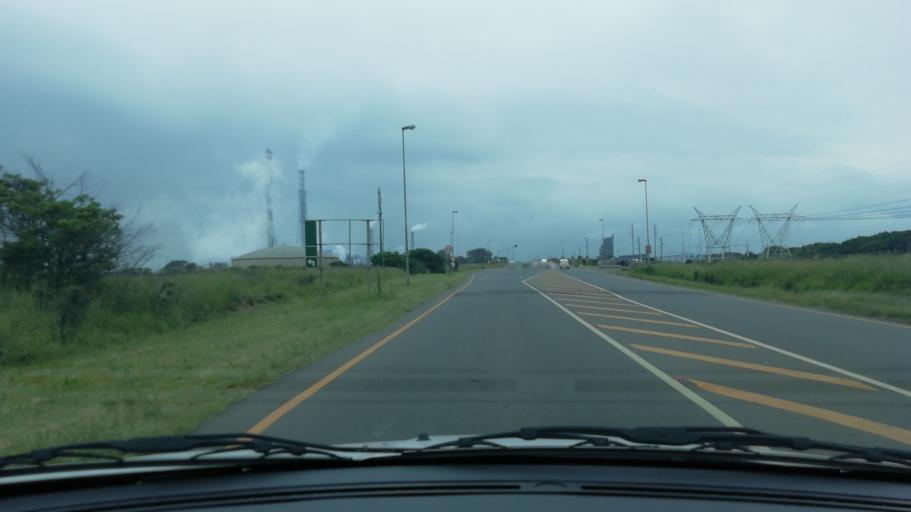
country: ZA
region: KwaZulu-Natal
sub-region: uThungulu District Municipality
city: Richards Bay
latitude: -28.7667
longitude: 32.0365
